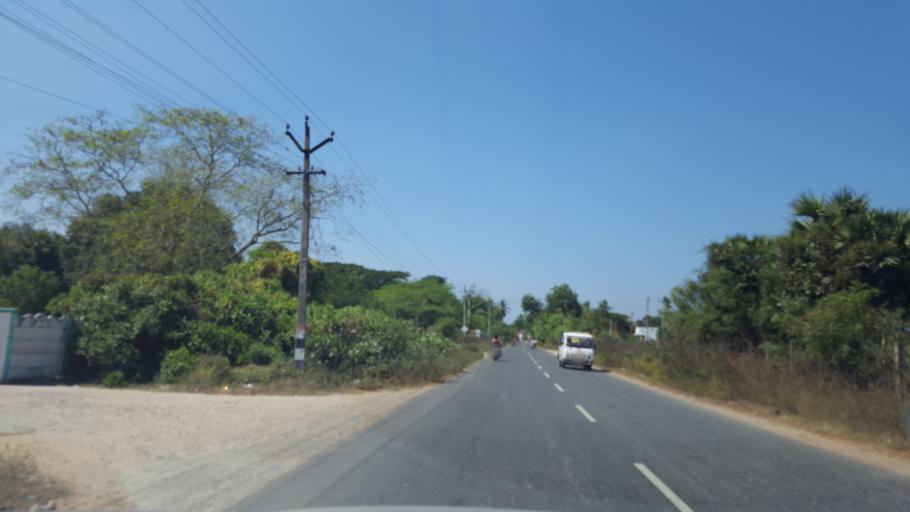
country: IN
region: Tamil Nadu
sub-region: Kancheepuram
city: Chengalpattu
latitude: 12.7248
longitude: 79.9516
